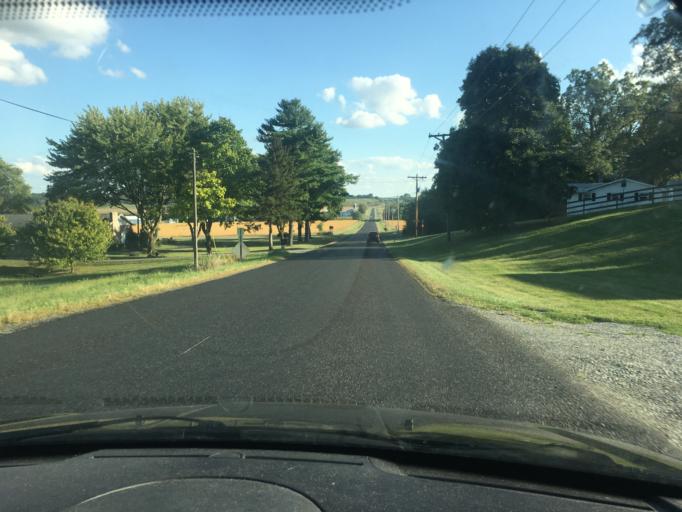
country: US
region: Ohio
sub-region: Logan County
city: West Liberty
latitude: 40.2868
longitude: -83.7278
